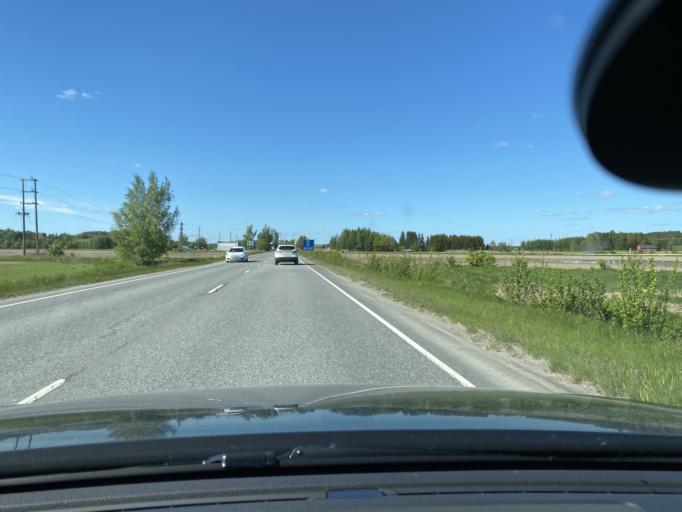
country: FI
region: Varsinais-Suomi
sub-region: Turku
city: Paimio
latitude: 60.4162
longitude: 22.6638
